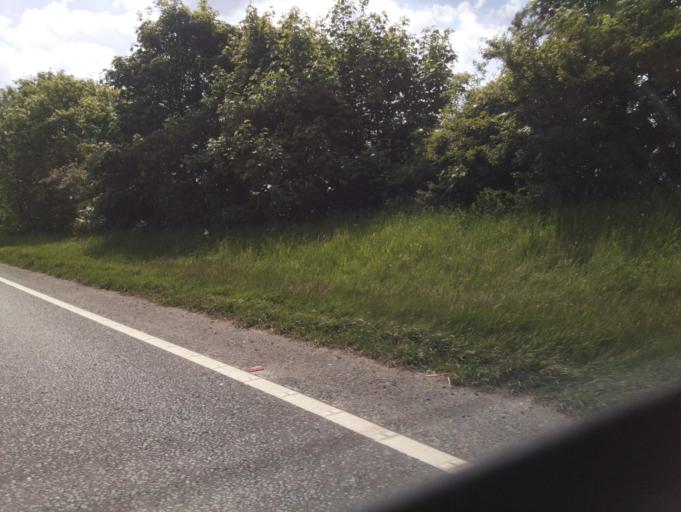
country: GB
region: England
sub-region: Hartlepool
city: Elwick
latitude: 54.6625
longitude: -1.3034
